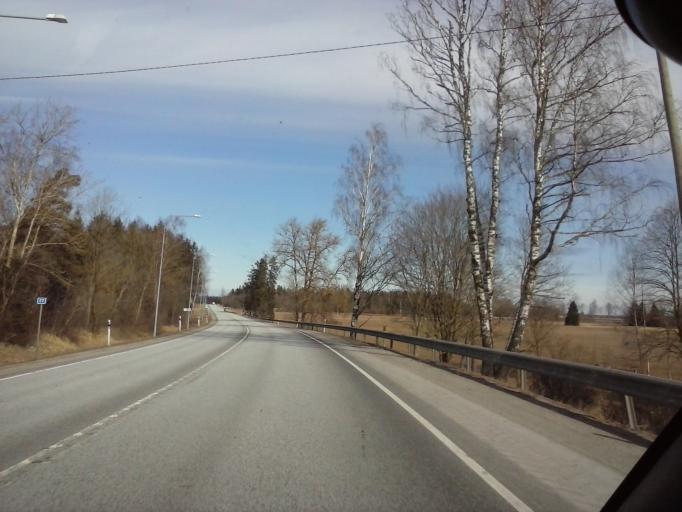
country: EE
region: Jaervamaa
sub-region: Paide linn
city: Paide
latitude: 59.0100
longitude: 25.5949
